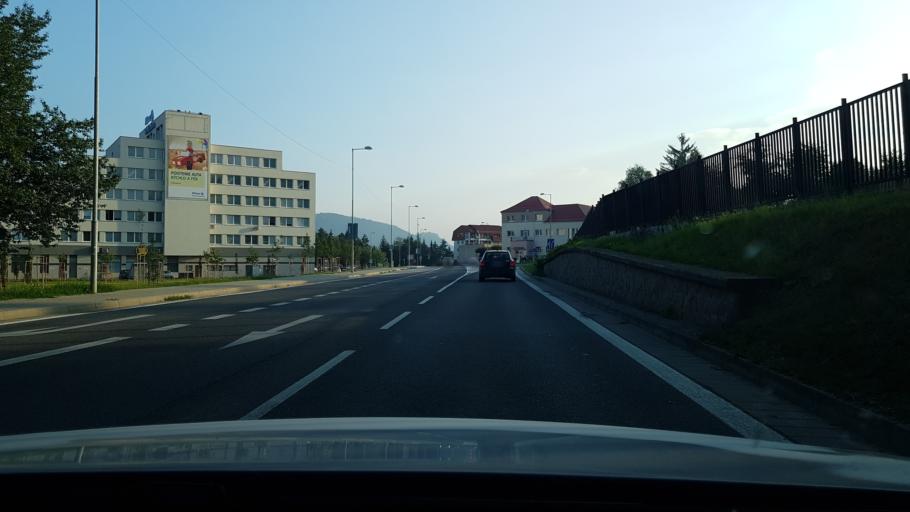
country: SK
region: Trenciansky
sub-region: Okres Povazska Bystrica
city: Povazska Bystrica
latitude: 49.1159
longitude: 18.4513
